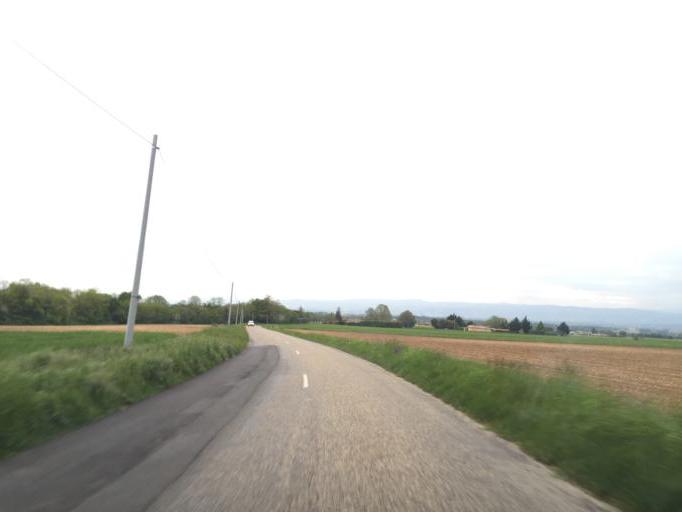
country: FR
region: Rhone-Alpes
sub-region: Departement de la Drome
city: Chatuzange-le-Goubet
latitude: 44.9476
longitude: 5.1058
